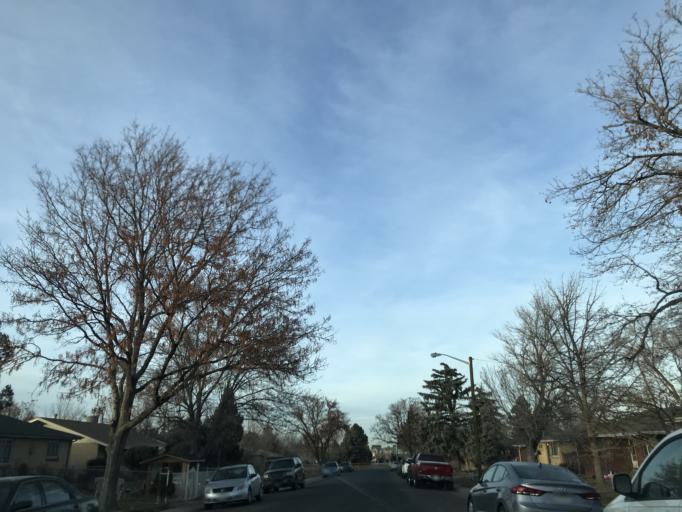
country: US
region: Colorado
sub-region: Adams County
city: Aurora
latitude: 39.7498
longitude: -104.8658
